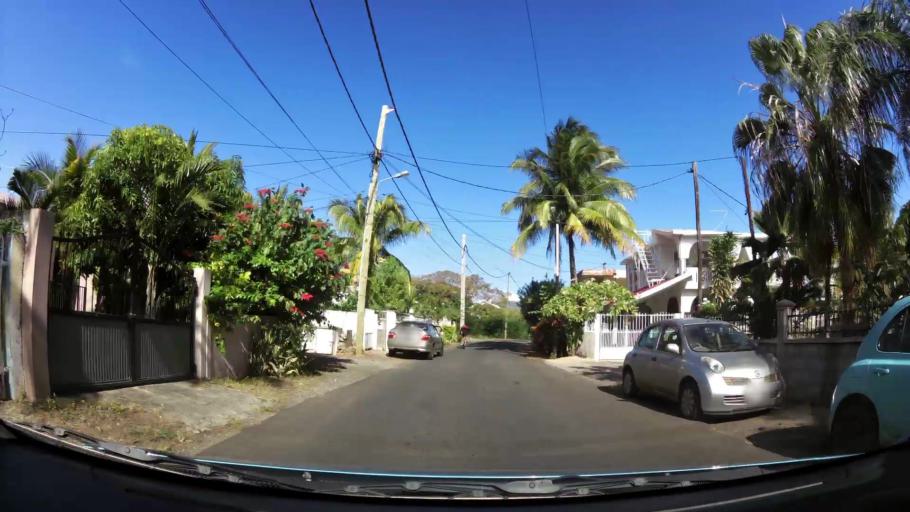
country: MU
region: Black River
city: Albion
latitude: -20.2050
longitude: 57.4064
